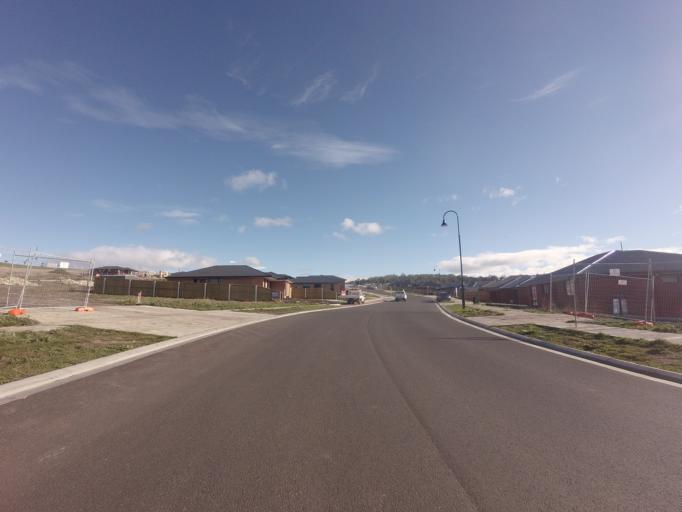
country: AU
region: Tasmania
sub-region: Clarence
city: Rokeby
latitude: -42.8869
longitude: 147.4318
